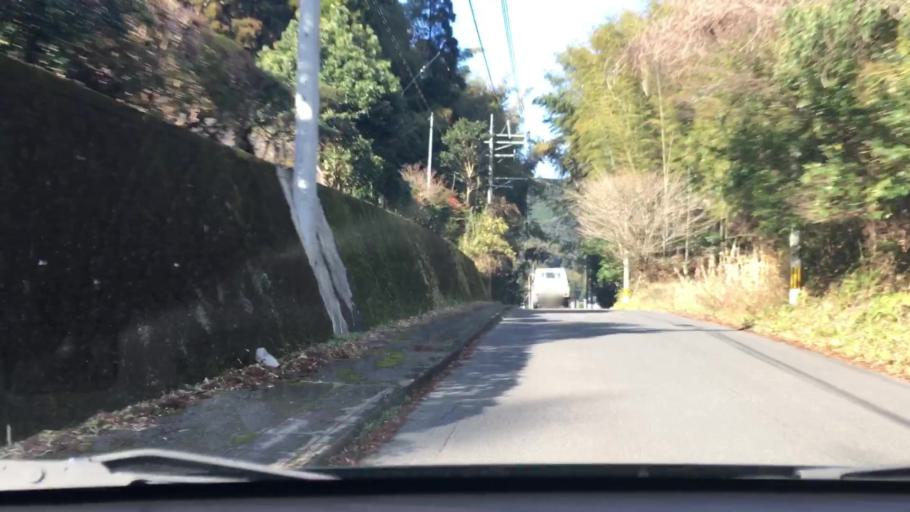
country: JP
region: Kagoshima
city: Ijuin
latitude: 31.7367
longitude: 130.4118
